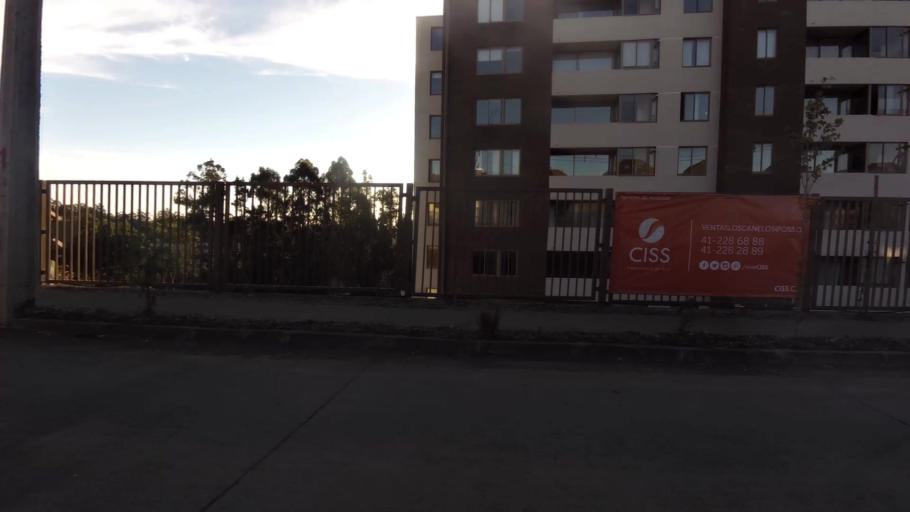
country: CL
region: Biobio
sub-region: Provincia de Concepcion
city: Concepcion
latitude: -36.8562
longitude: -73.0923
